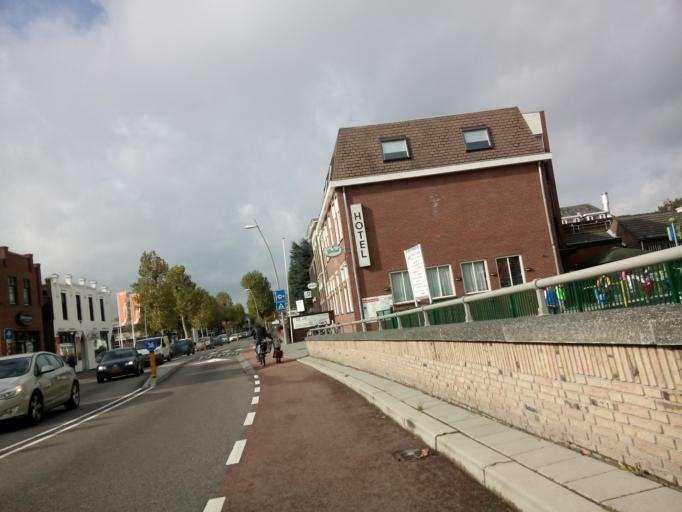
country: NL
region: South Holland
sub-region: Gemeente Waddinxveen
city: Oranjewijk
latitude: 52.0442
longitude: 4.6577
